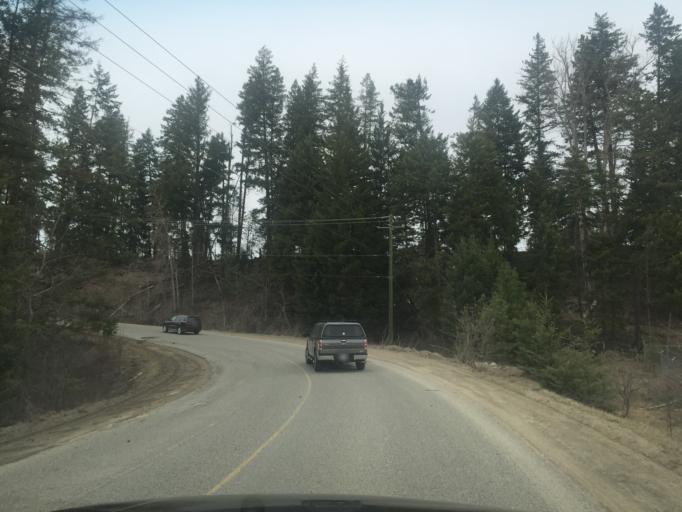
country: CA
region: British Columbia
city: Kamloops
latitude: 51.1951
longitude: -120.1295
